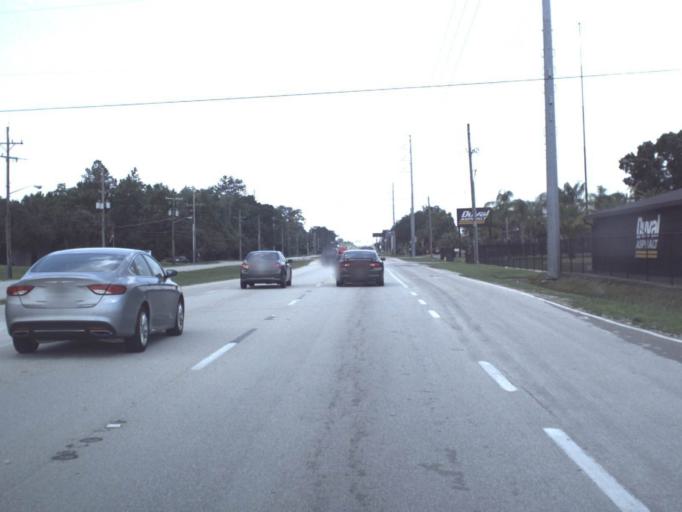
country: US
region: Florida
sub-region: Duval County
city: Jacksonville
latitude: 30.2364
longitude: -81.5947
